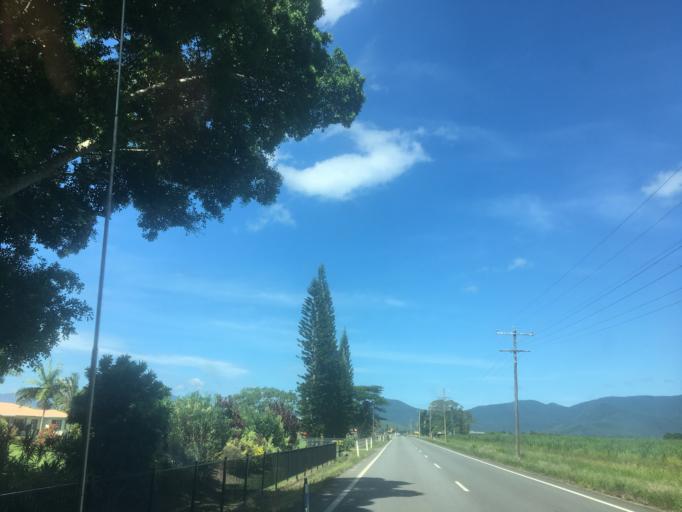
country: AU
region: Queensland
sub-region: Cairns
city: Woree
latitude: -17.0624
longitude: 145.7600
